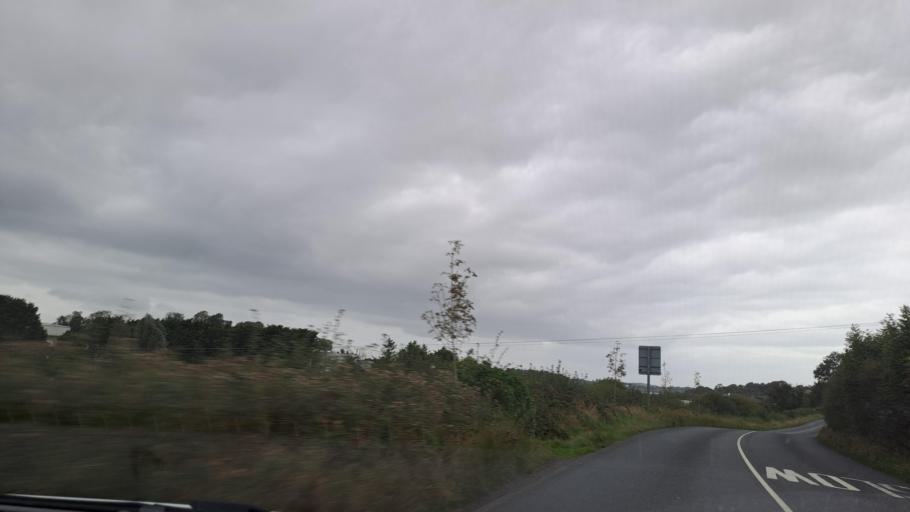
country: IE
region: Ulster
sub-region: An Cabhan
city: Bailieborough
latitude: 53.9983
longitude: -6.8996
